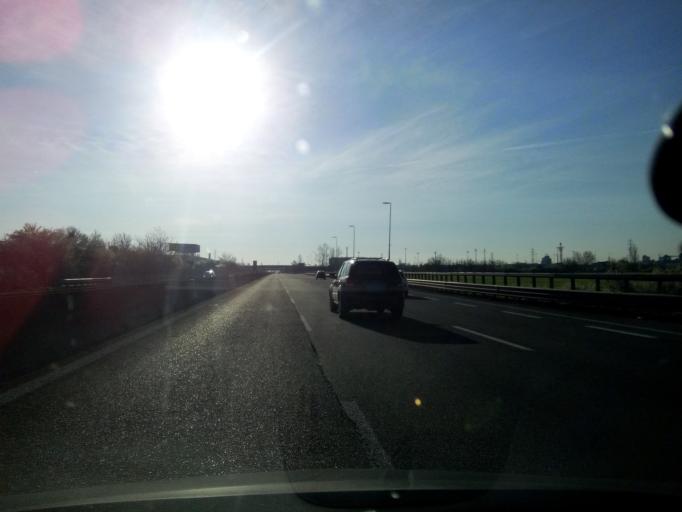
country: IT
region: Emilia-Romagna
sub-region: Provincia di Parma
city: Baganzola
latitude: 44.8420
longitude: 10.3299
